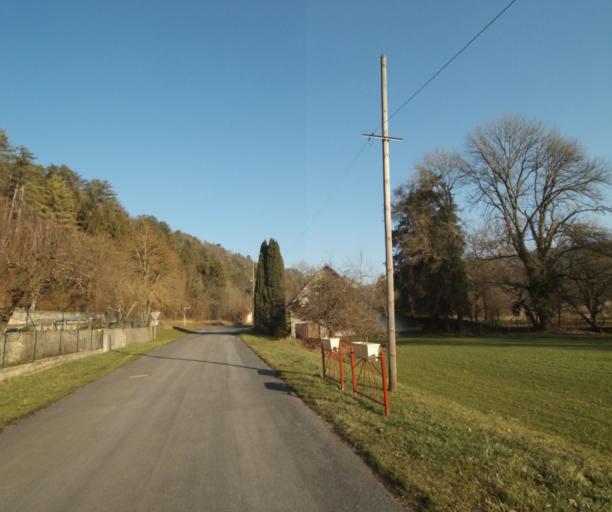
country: FR
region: Champagne-Ardenne
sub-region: Departement de la Haute-Marne
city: Chevillon
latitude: 48.4934
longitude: 5.1393
